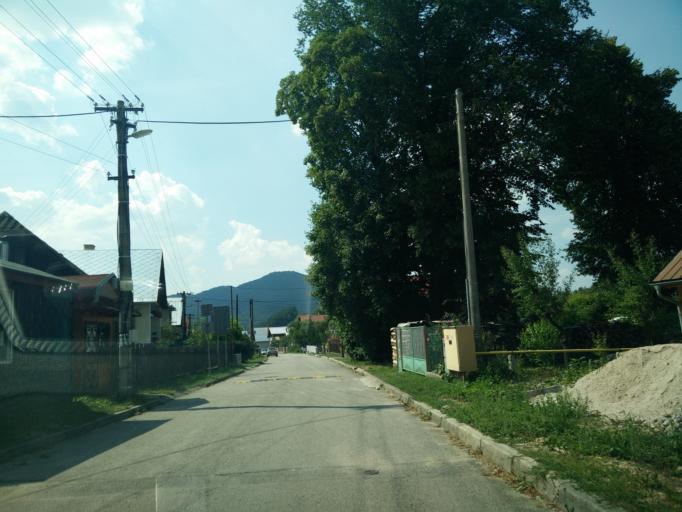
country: SK
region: Zilinsky
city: Rajec
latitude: 49.0439
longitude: 18.6345
